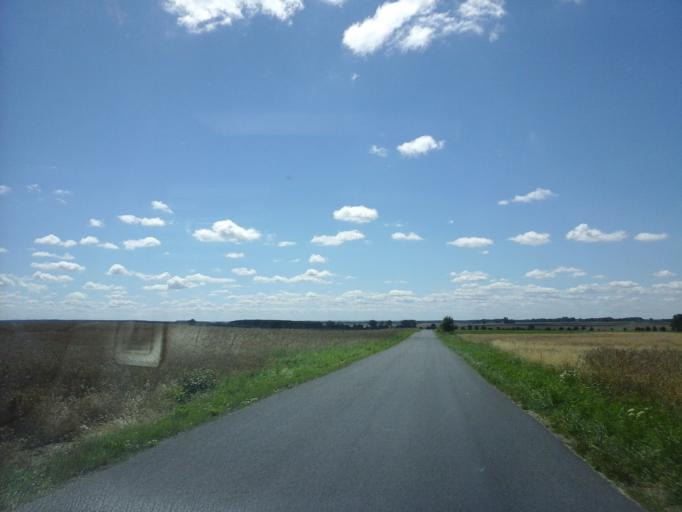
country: PL
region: West Pomeranian Voivodeship
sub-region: Powiat choszczenski
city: Recz
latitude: 53.2843
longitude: 15.4940
